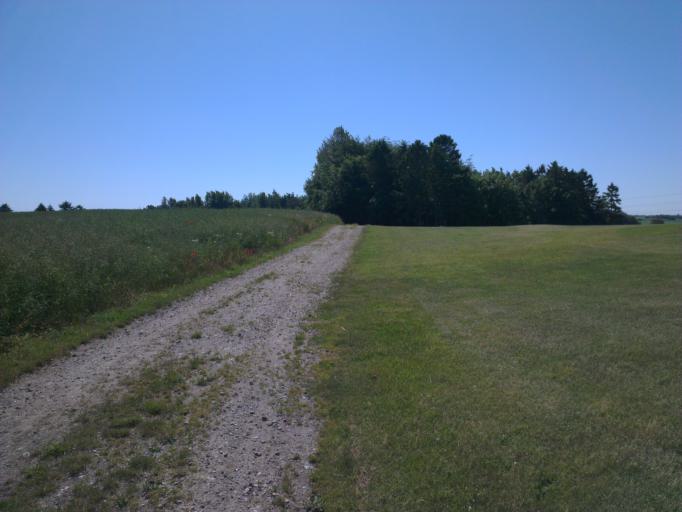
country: DK
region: Capital Region
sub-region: Frederikssund Kommune
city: Jaegerspris
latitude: 55.8123
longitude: 11.9249
